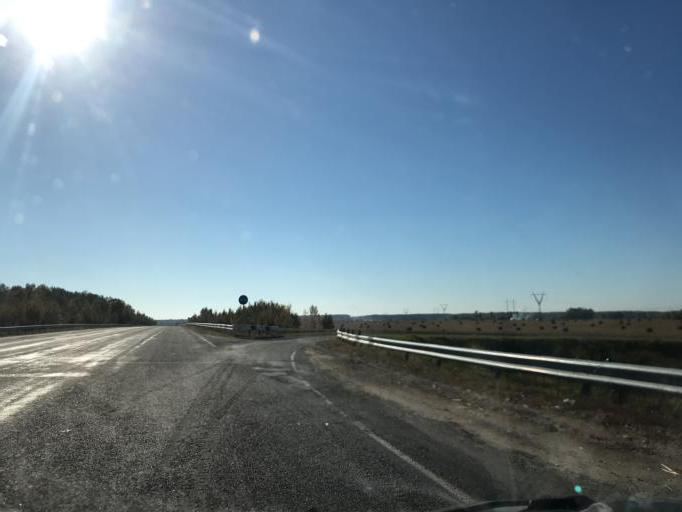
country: BY
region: Mogilev
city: Babruysk
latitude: 53.1052
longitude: 29.0565
